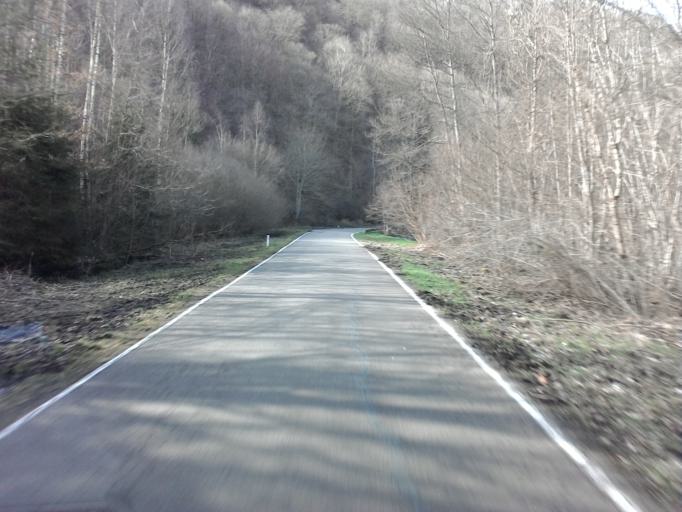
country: BE
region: Wallonia
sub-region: Province du Luxembourg
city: Daverdisse
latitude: 50.0455
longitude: 5.1334
